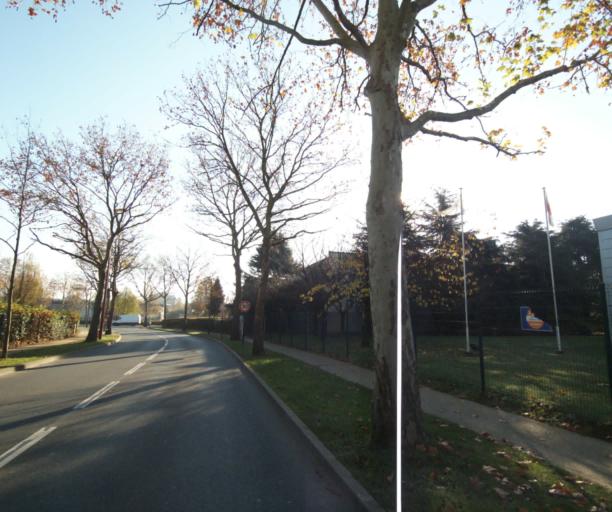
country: FR
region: Ile-de-France
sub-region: Departement du Val-d'Oise
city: Gonesse
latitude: 48.9908
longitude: 2.4344
